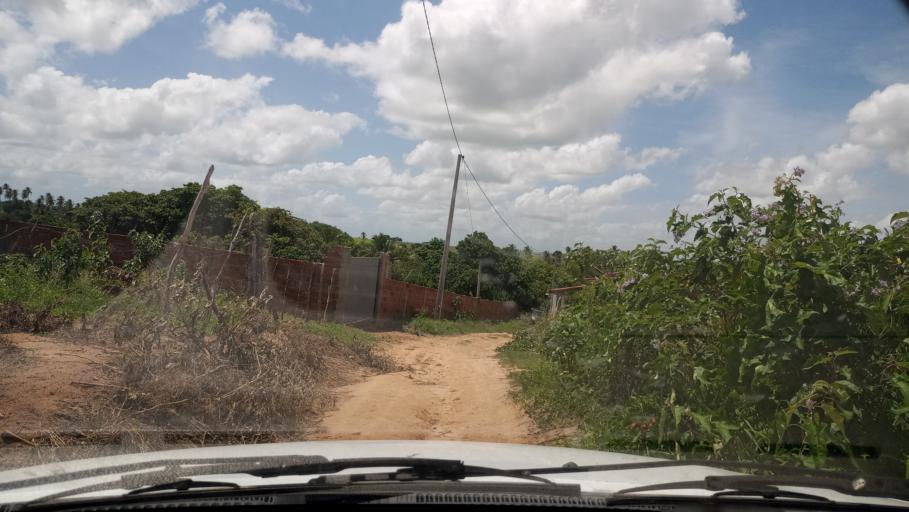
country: BR
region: Rio Grande do Norte
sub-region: Brejinho
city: Brejinho
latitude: -6.2660
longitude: -35.3711
